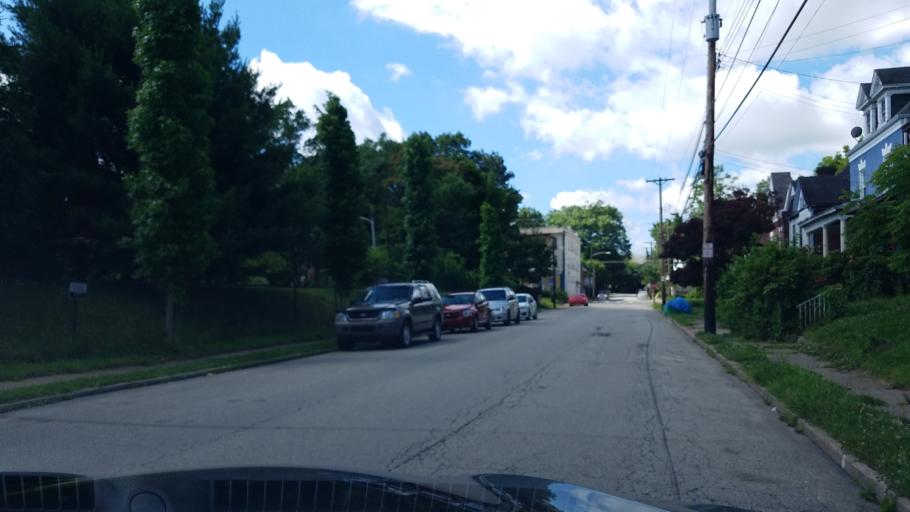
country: US
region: Pennsylvania
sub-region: Allegheny County
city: Wilkinsburg
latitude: 40.4370
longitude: -79.8822
